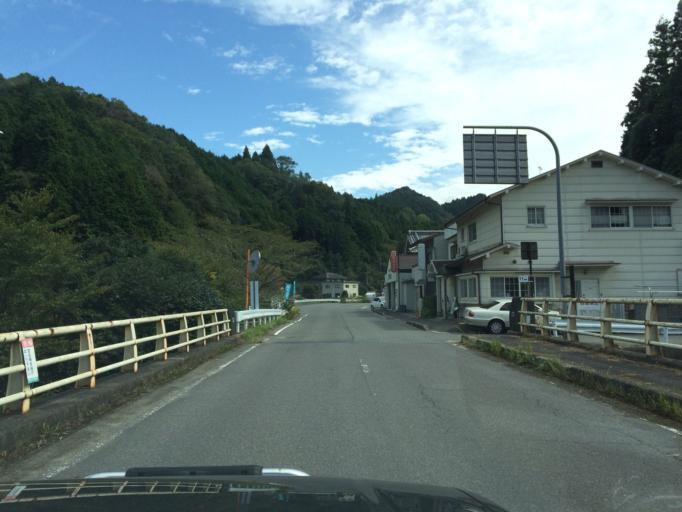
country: JP
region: Mie
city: Nabari
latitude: 34.6799
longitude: 135.9754
